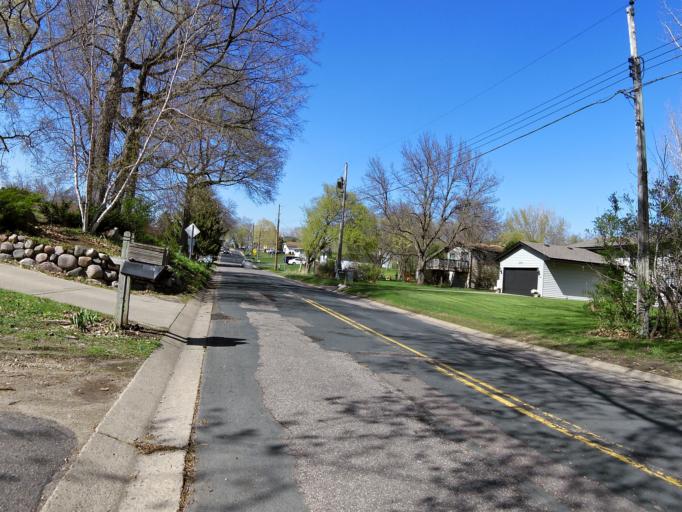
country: US
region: Minnesota
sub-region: Scott County
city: Prior Lake
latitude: 44.7111
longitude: -93.4385
